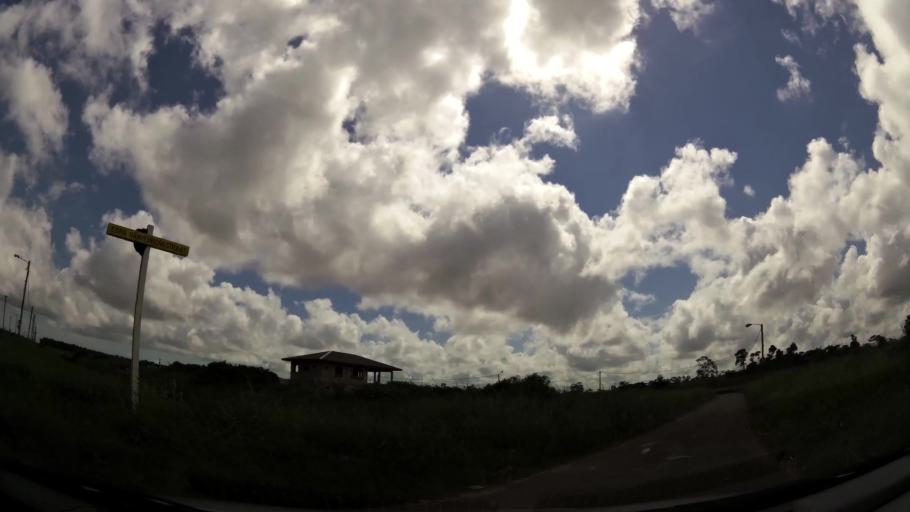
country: SR
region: Paramaribo
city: Paramaribo
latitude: 5.8733
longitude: -55.1309
